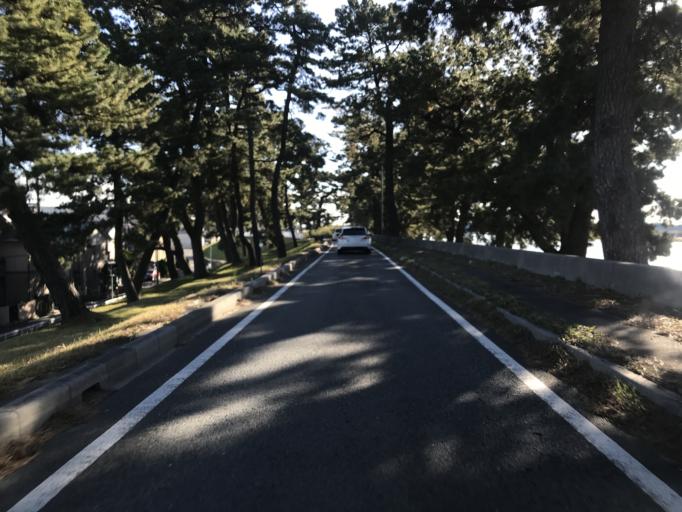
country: JP
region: Aichi
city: Kanie
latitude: 35.1271
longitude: 136.8387
